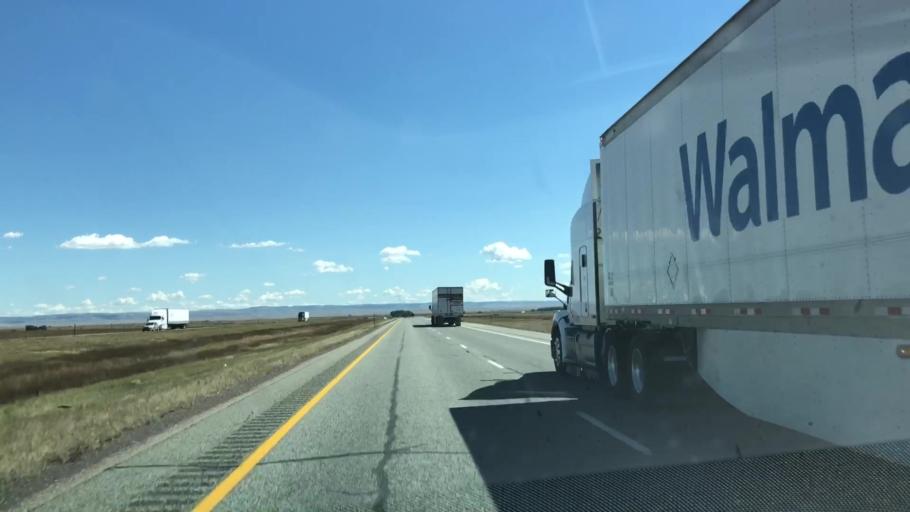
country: US
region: Wyoming
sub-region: Albany County
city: Laramie
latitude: 41.4178
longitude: -105.8559
